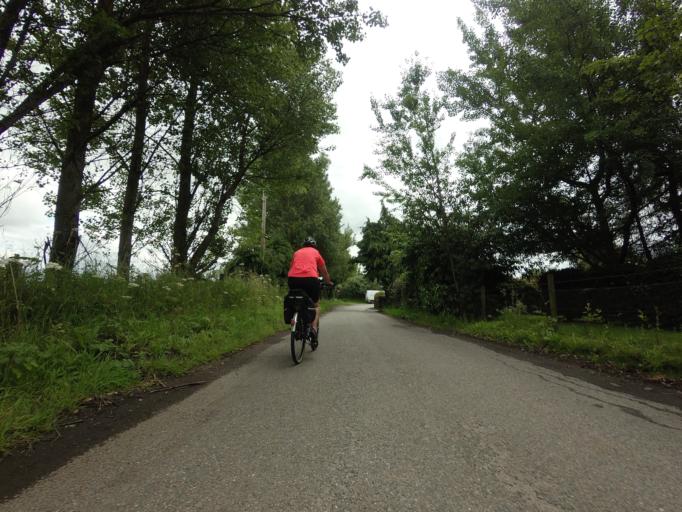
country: GB
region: Scotland
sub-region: Moray
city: Forres
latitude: 57.6151
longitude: -3.6193
